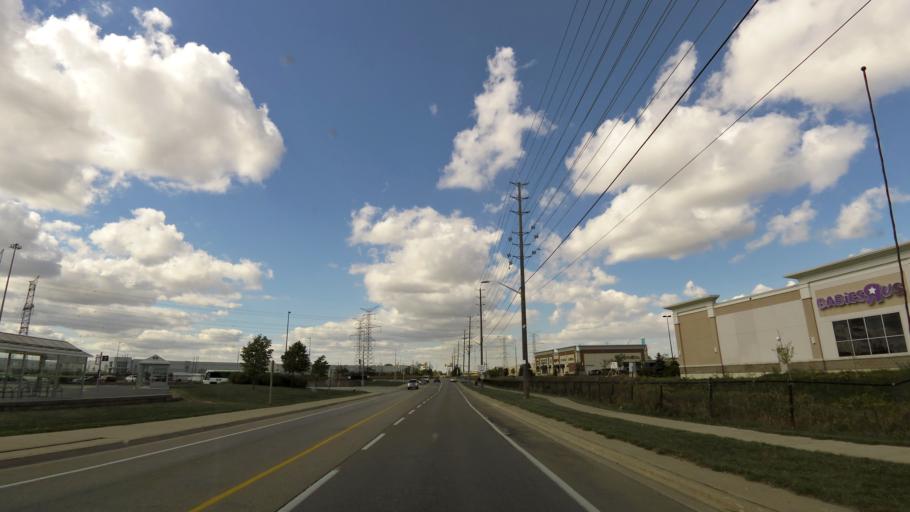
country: CA
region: Ontario
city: Brampton
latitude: 43.5919
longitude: -79.7874
